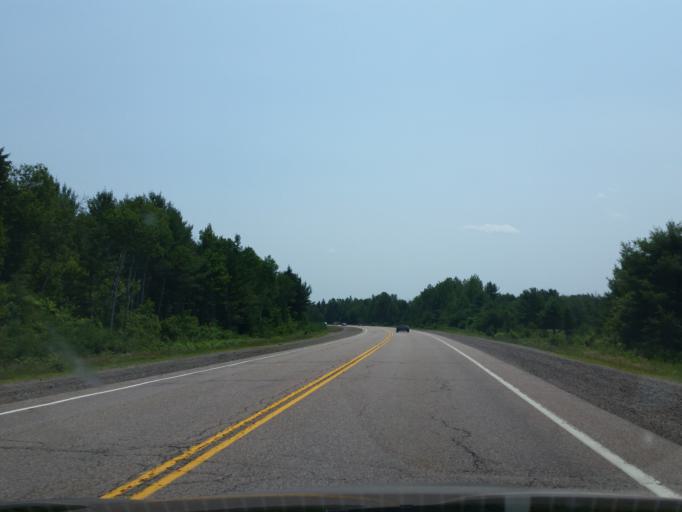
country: CA
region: Ontario
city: Petawawa
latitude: 45.8510
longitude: -77.2797
